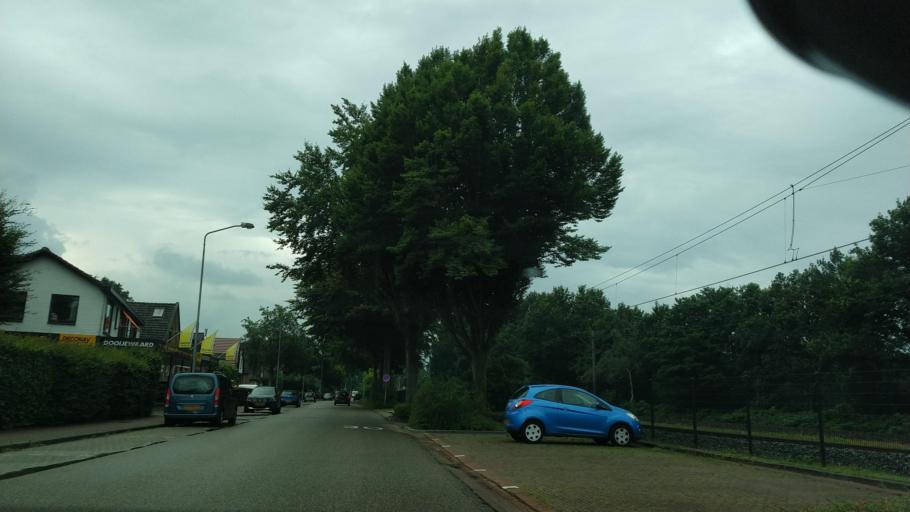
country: NL
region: Gelderland
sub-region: Gemeente Ermelo
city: Ermelo
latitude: 52.2998
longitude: 5.6138
